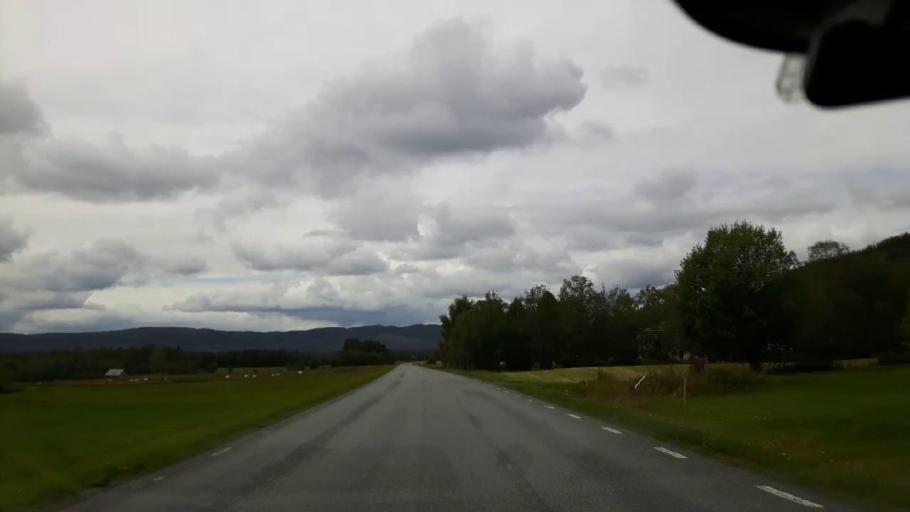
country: SE
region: Jaemtland
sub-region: Krokoms Kommun
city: Krokom
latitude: 63.4546
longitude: 14.1501
